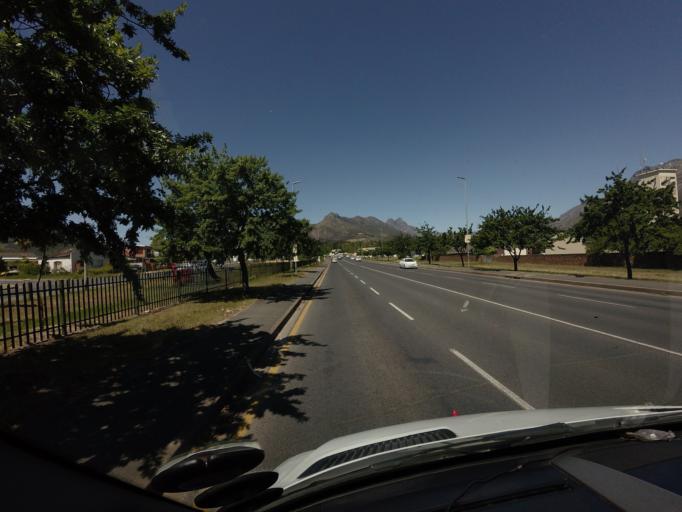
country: ZA
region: Western Cape
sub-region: Cape Winelands District Municipality
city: Stellenbosch
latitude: -33.9247
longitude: 18.8750
